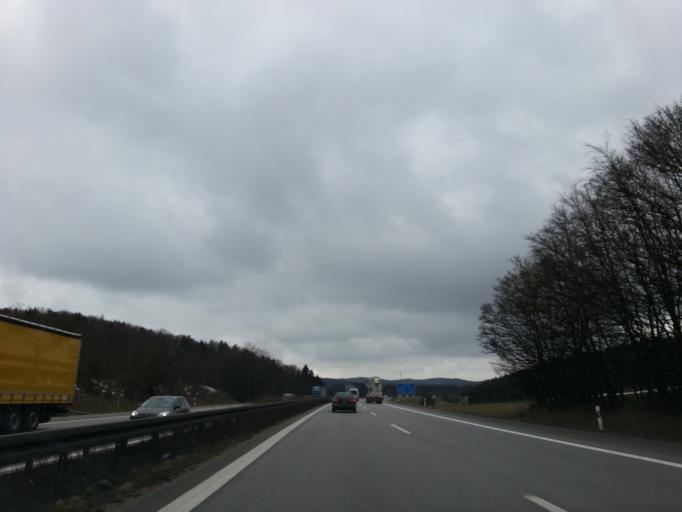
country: DE
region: Bavaria
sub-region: Upper Palatinate
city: Hohenfels
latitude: 49.1482
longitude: 11.8508
